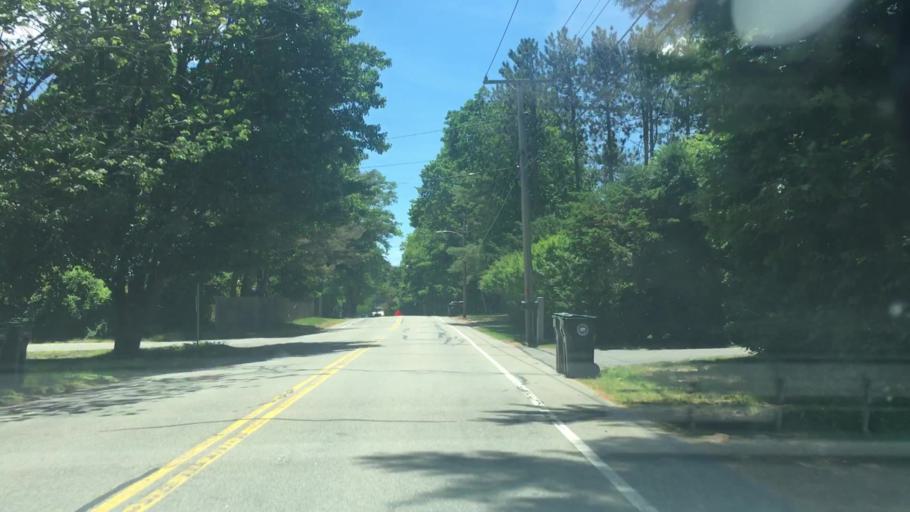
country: US
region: Maine
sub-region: York County
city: Kennebunk
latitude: 43.3700
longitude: -70.5260
